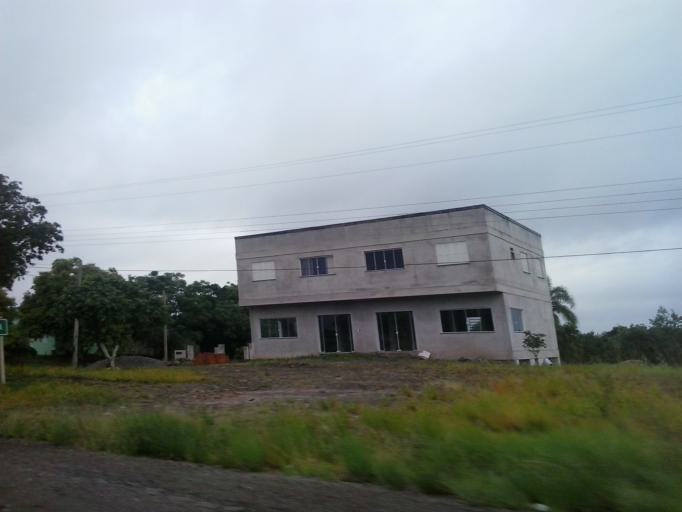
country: BR
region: Rio Grande do Sul
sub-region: Santa Maria
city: Santa Maria
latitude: -29.7226
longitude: -53.3874
